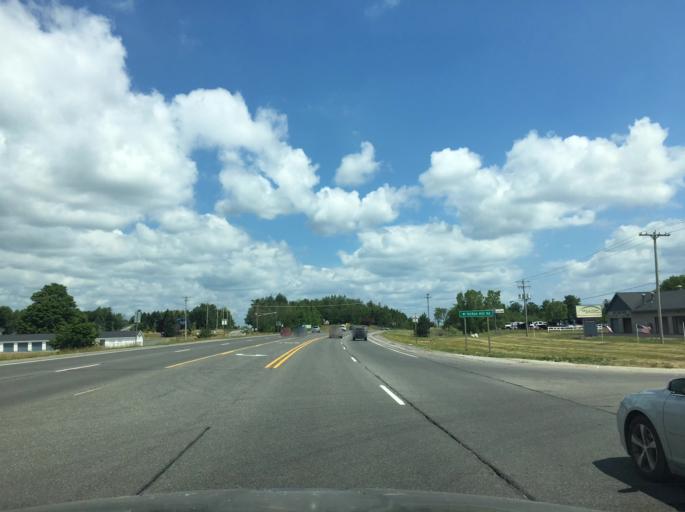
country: US
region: Michigan
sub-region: Grand Traverse County
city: Traverse City
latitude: 44.6994
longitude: -85.6562
